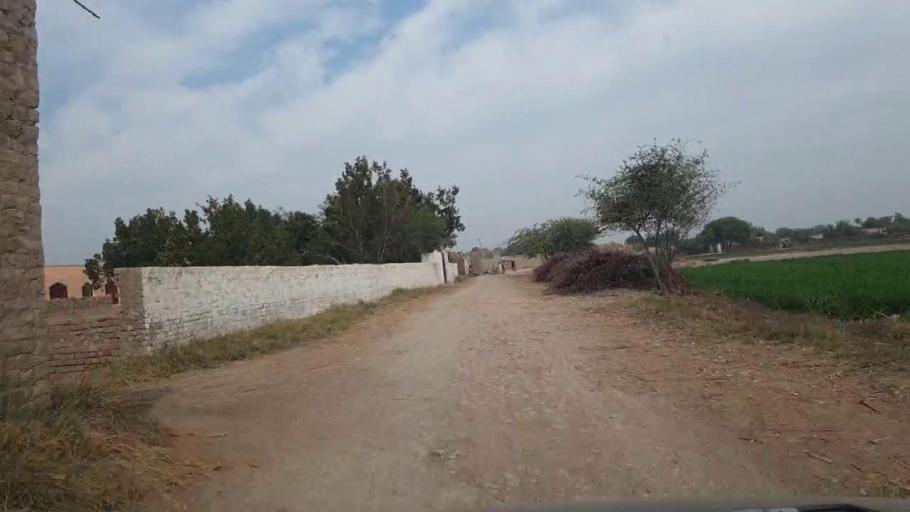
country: PK
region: Sindh
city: Shahdadpur
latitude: 25.9403
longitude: 68.6827
